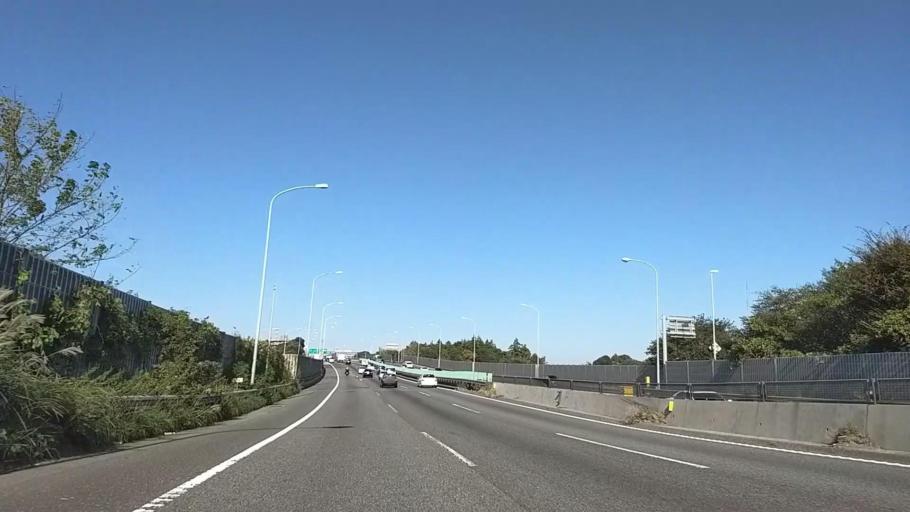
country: JP
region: Kanagawa
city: Minami-rinkan
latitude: 35.4616
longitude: 139.5431
